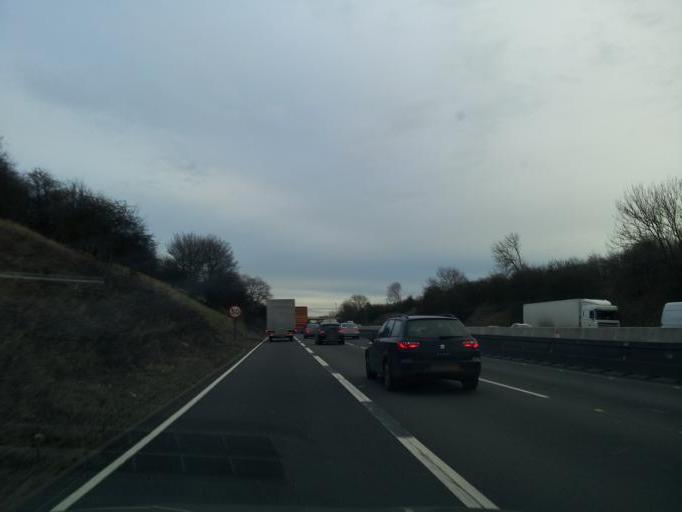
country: GB
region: England
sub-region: Northamptonshire
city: Long Buckby
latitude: 52.2477
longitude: -1.0639
